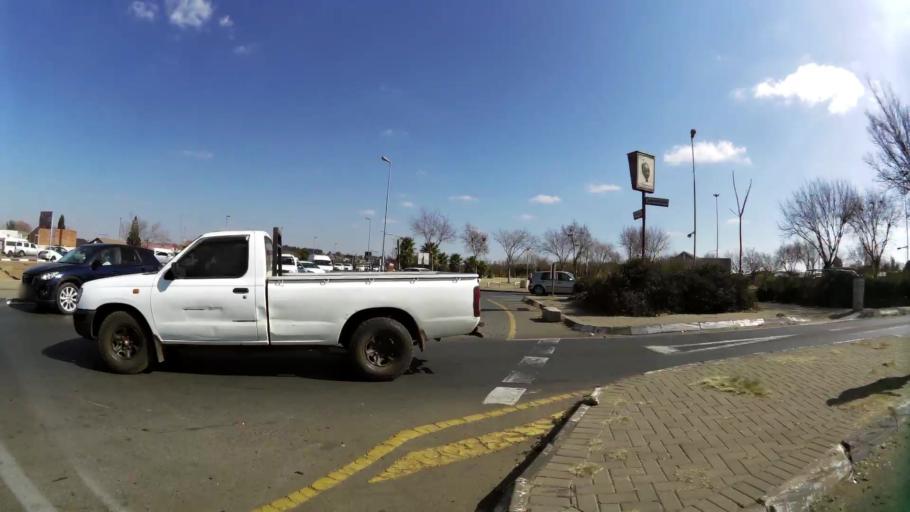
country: ZA
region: Gauteng
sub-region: City of Johannesburg Metropolitan Municipality
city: Soweto
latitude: -26.2629
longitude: 27.8850
